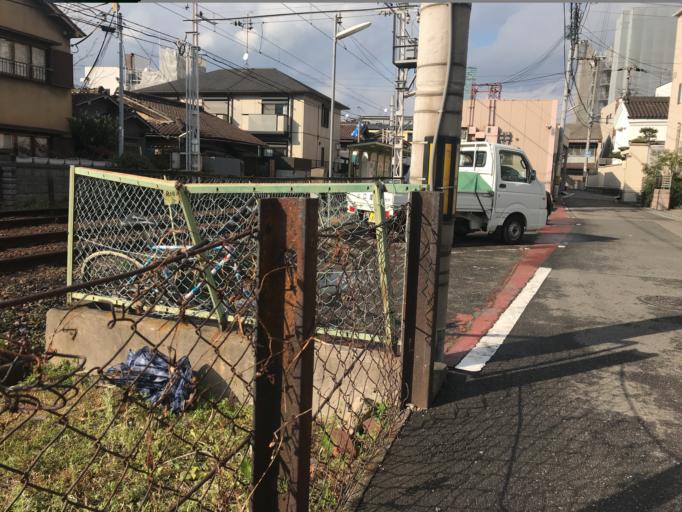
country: JP
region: Osaka
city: Osaka-shi
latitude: 34.6322
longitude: 135.5084
